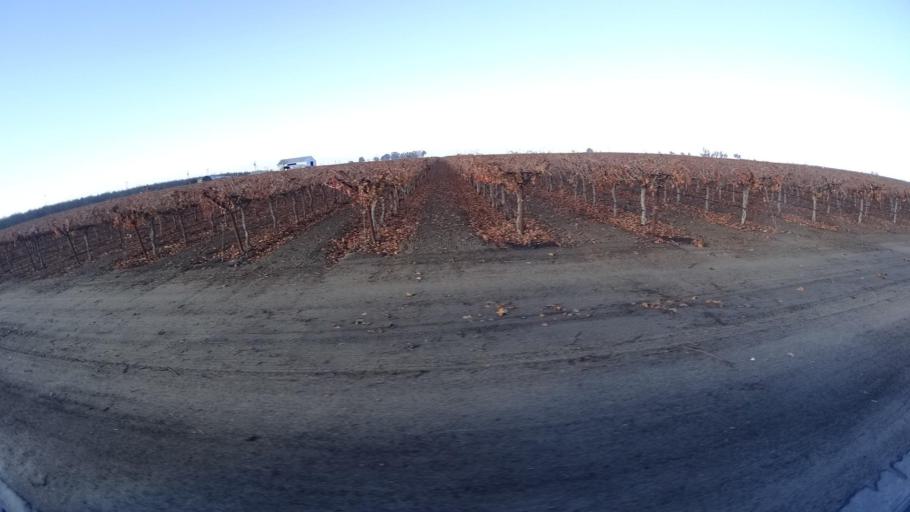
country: US
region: California
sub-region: Kern County
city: Delano
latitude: 35.7336
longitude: -119.3302
